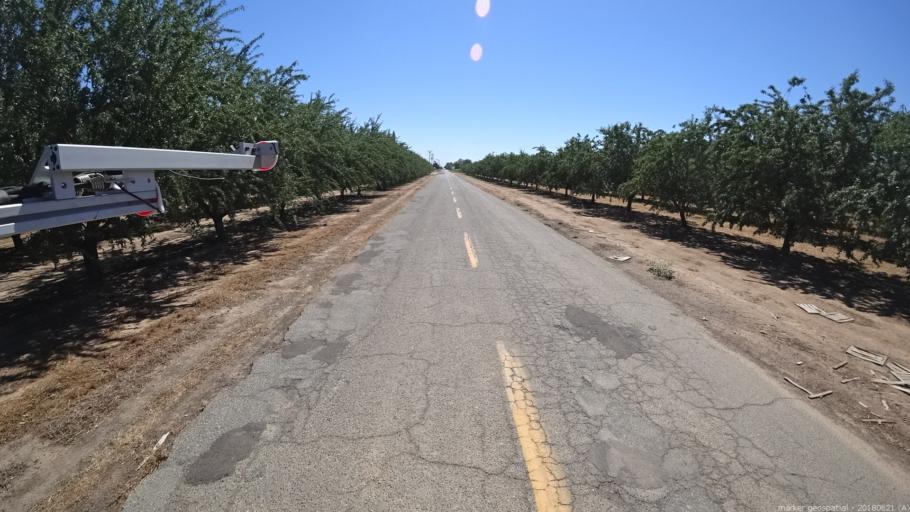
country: US
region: California
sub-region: Madera County
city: Parksdale
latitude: 36.9094
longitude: -119.9670
